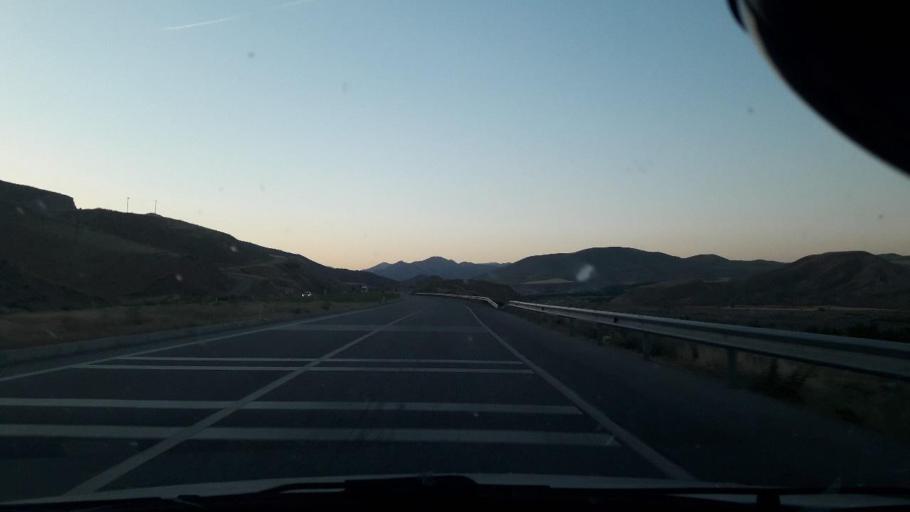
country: TR
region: Malatya
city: Yazihan
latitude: 38.6344
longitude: 38.1594
